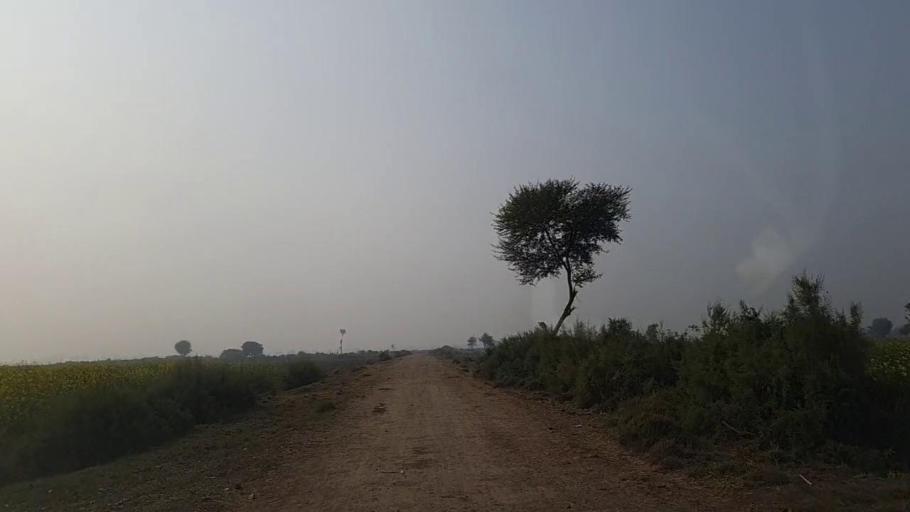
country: PK
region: Sindh
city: Sanghar
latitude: 26.0870
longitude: 68.9167
